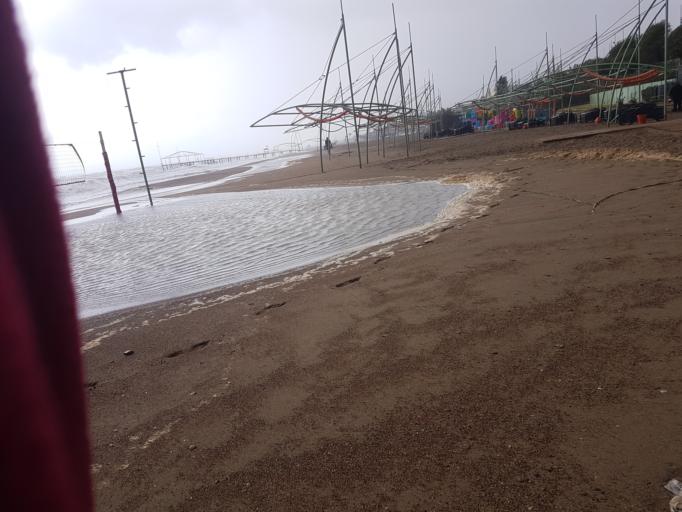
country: TR
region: Antalya
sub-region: Serik
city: Kumkoey
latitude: 36.8532
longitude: 30.8815
